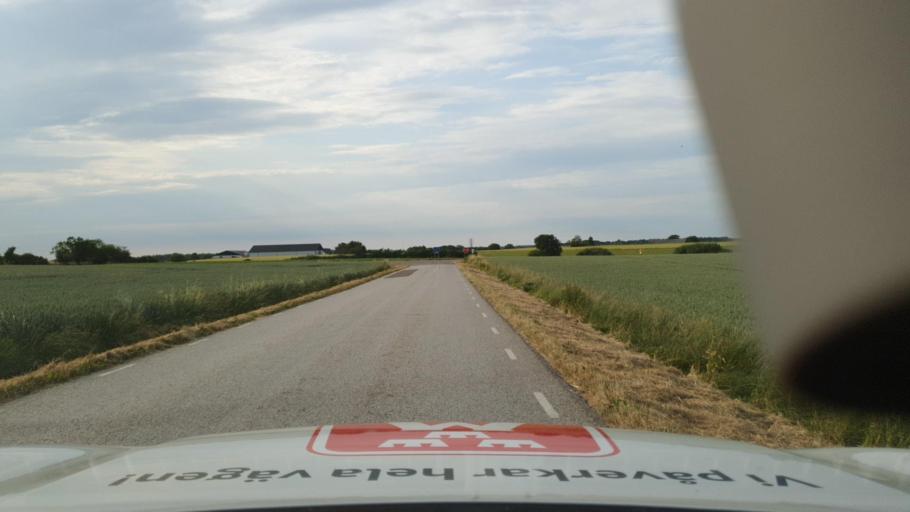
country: SE
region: Skane
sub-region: Sjobo Kommun
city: Sjoebo
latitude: 55.6513
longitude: 13.8132
